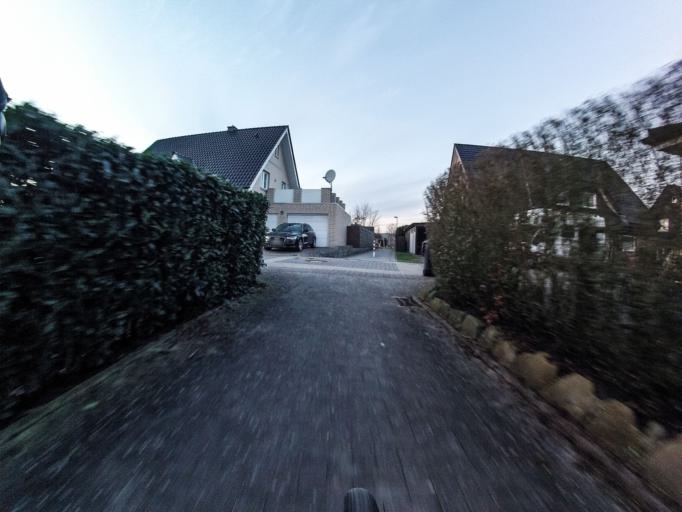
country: DE
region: North Rhine-Westphalia
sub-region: Regierungsbezirk Munster
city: Tecklenburg
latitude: 52.2638
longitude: 7.7947
